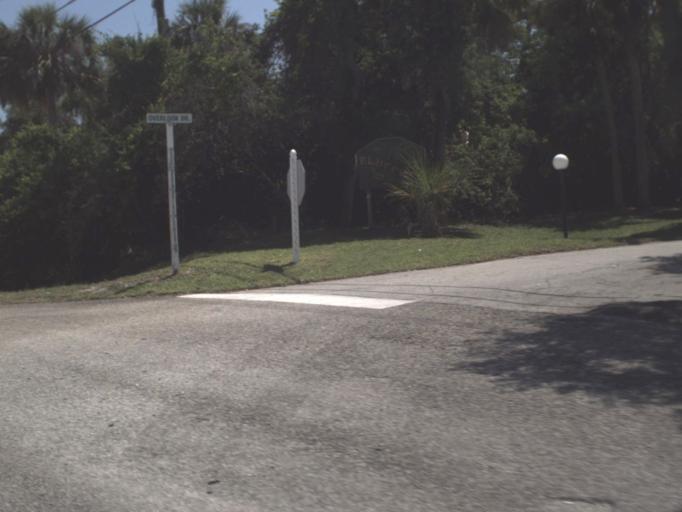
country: US
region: Florida
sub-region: Brevard County
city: Malabar
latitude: 28.0141
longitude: -80.5678
